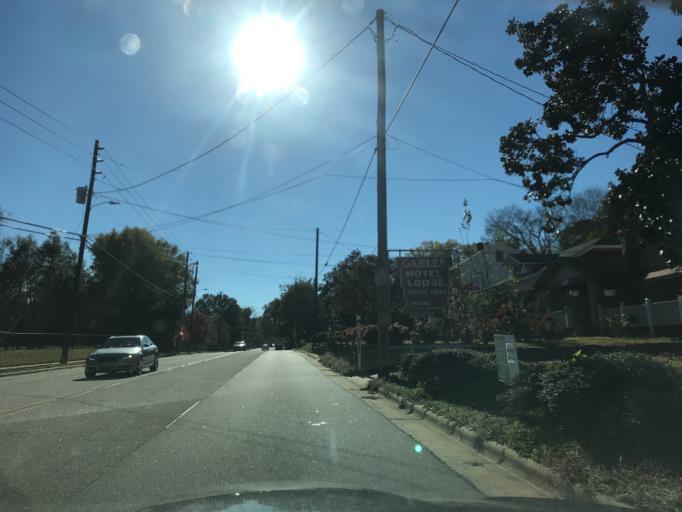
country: US
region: North Carolina
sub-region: Wake County
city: Raleigh
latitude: 35.7957
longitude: -78.6306
